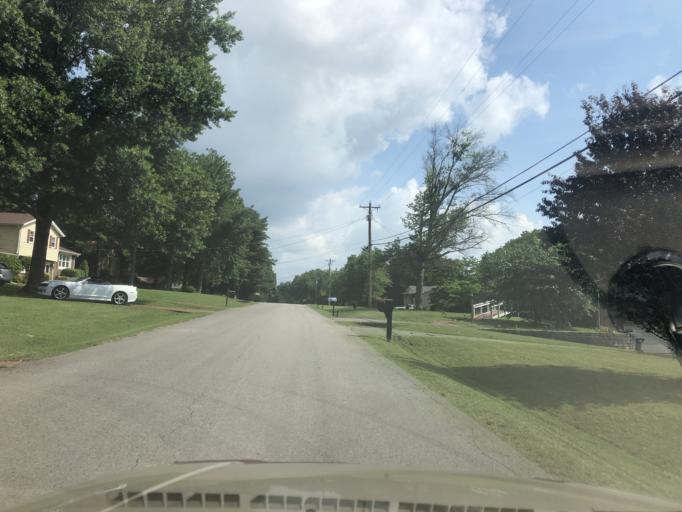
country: US
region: Tennessee
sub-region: Wilson County
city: Green Hill
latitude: 36.2359
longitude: -86.5876
